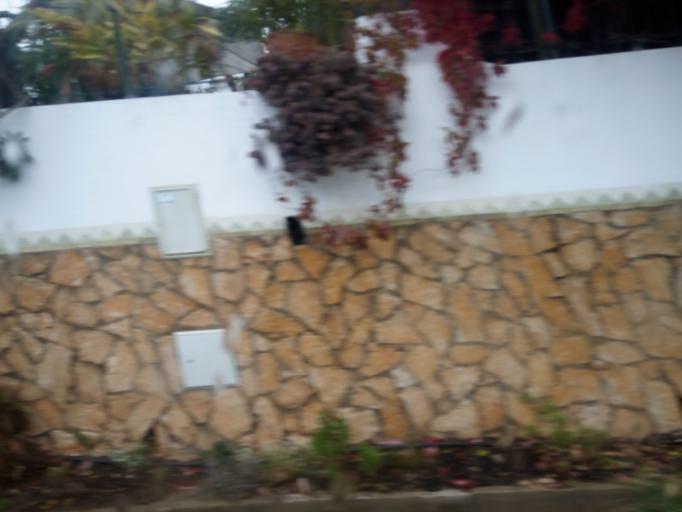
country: PT
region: Faro
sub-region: Faro
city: Santa Barbara de Nexe
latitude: 37.1056
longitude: -7.9798
